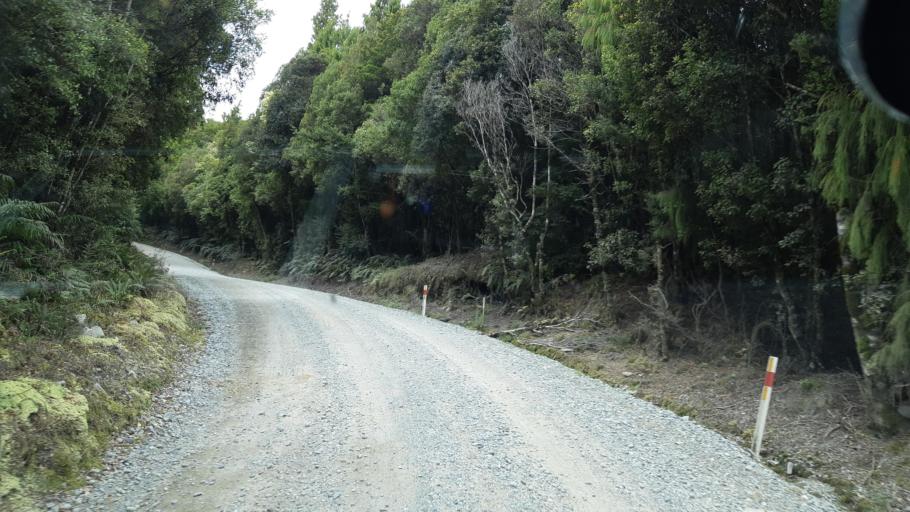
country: NZ
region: West Coast
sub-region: Grey District
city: Greymouth
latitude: -42.7297
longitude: 171.2336
